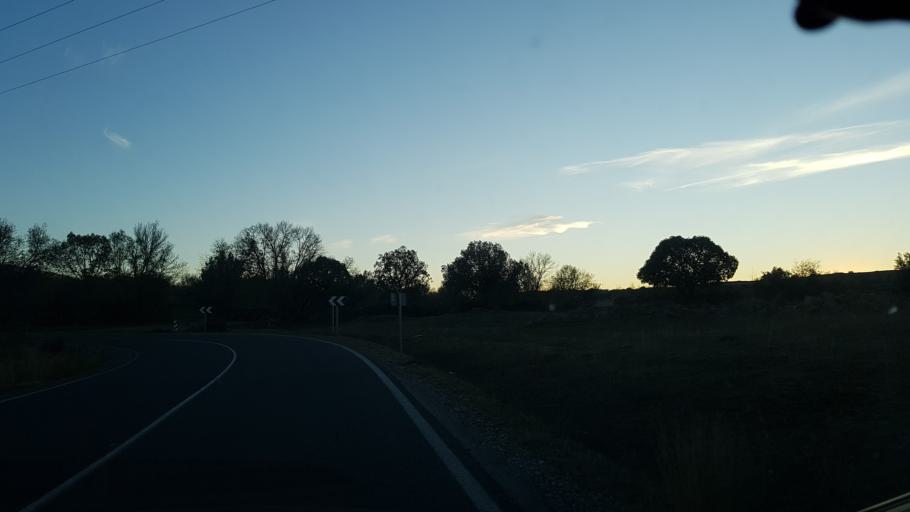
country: ES
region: Castille and Leon
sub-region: Provincia de Segovia
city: Ortigosa del Monte
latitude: 40.8610
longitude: -4.1780
